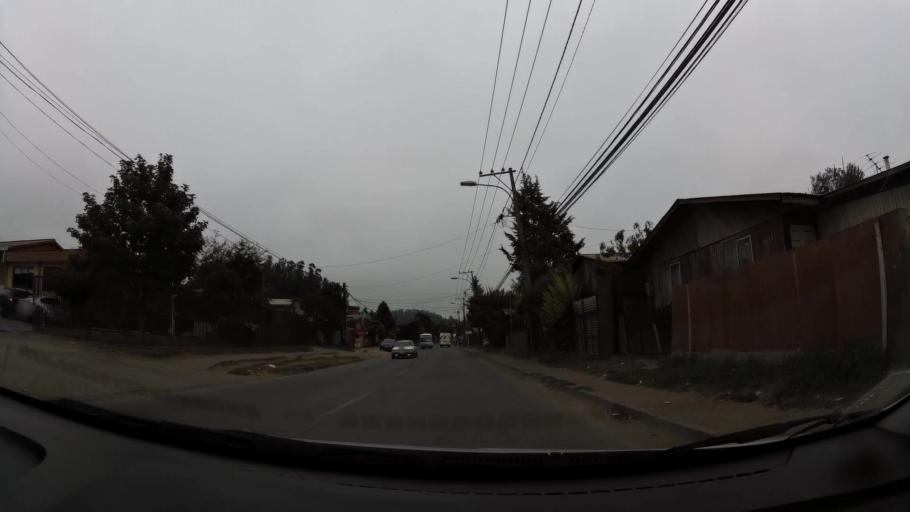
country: CL
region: Biobio
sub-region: Provincia de Concepcion
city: Concepcion
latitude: -36.8217
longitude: -73.0062
